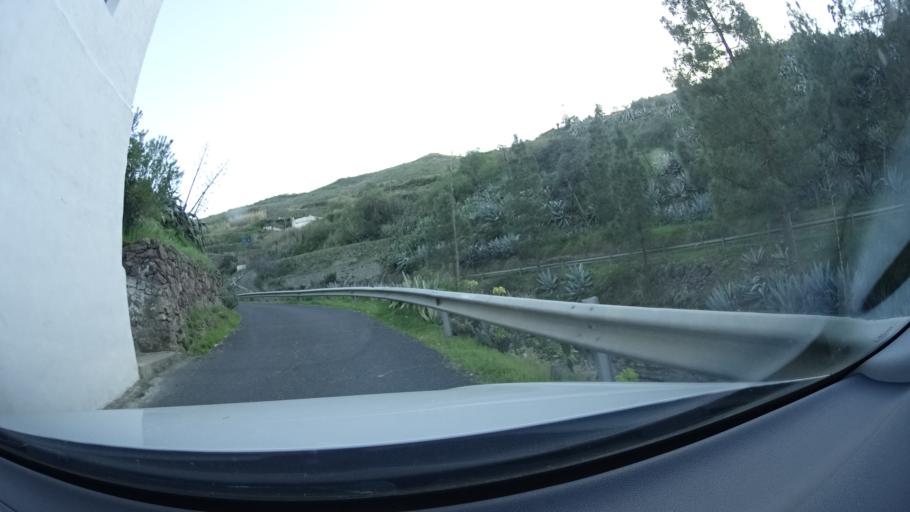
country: ES
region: Canary Islands
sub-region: Provincia de Las Palmas
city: Artenara
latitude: 28.0430
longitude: -15.6711
